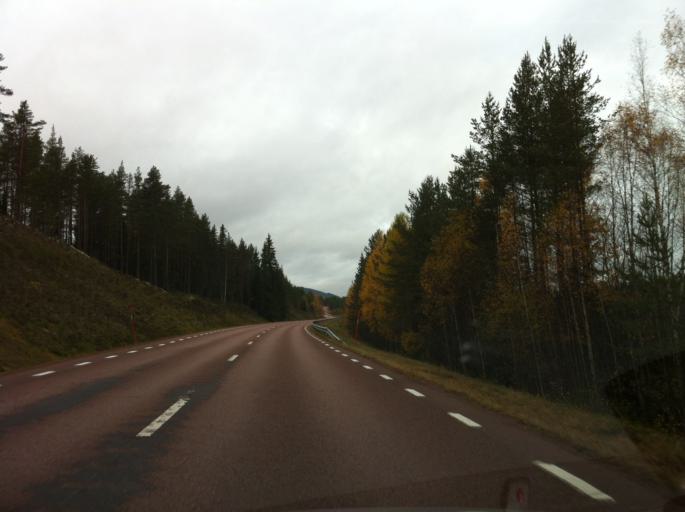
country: SE
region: Dalarna
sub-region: Alvdalens Kommun
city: AElvdalen
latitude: 61.2768
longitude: 13.7761
